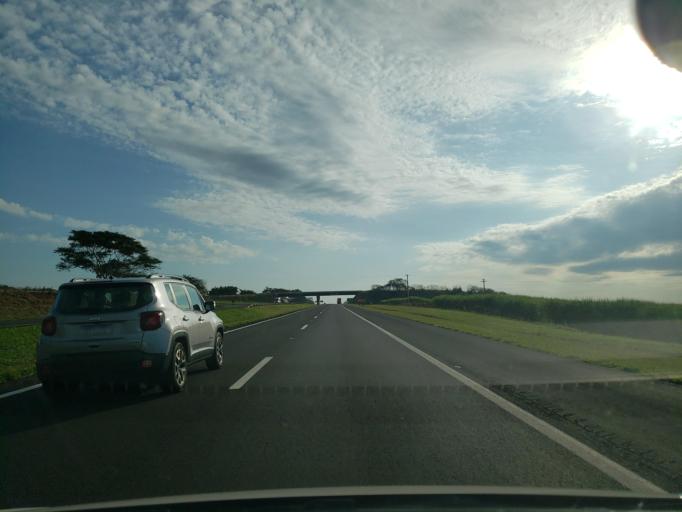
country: BR
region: Sao Paulo
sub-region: Valparaiso
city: Valparaiso
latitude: -21.2051
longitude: -50.7909
